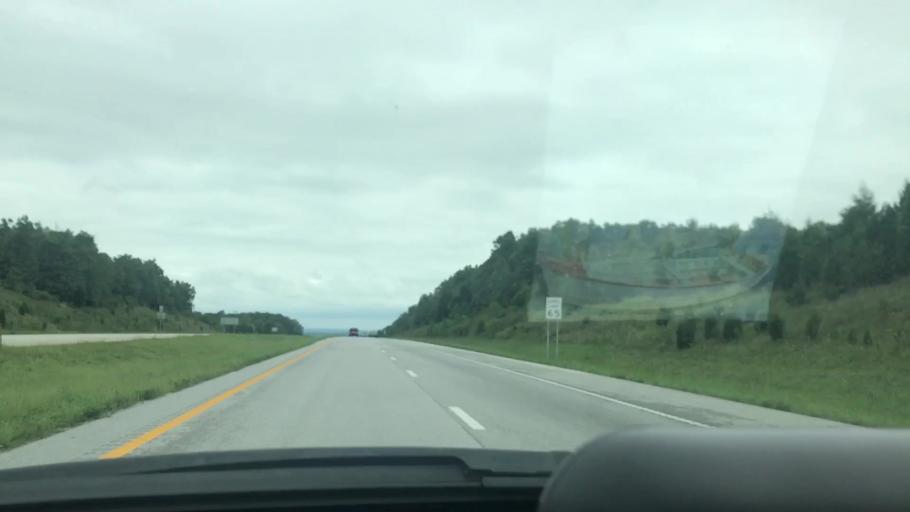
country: US
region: Missouri
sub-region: Greene County
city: Fair Grove
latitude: 37.3289
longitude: -93.1680
